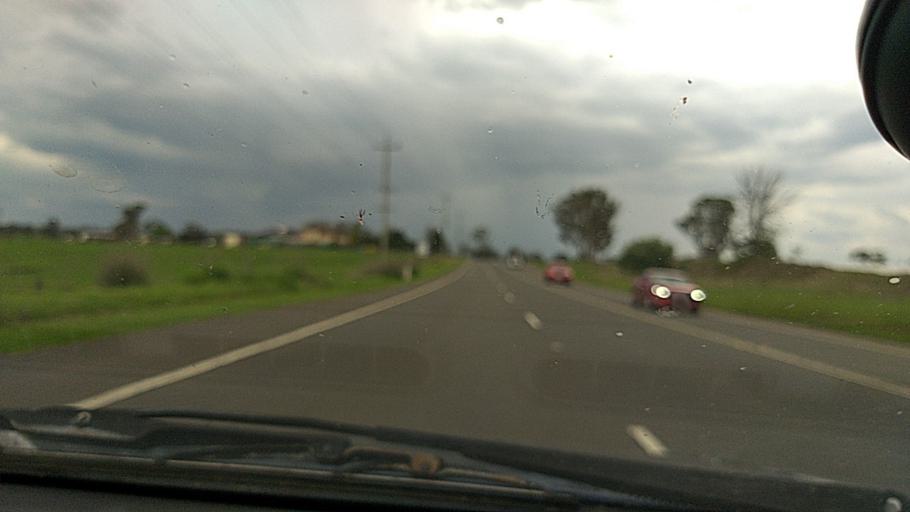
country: AU
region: New South Wales
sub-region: Liverpool
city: Luddenham
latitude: -33.8681
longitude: 150.6950
